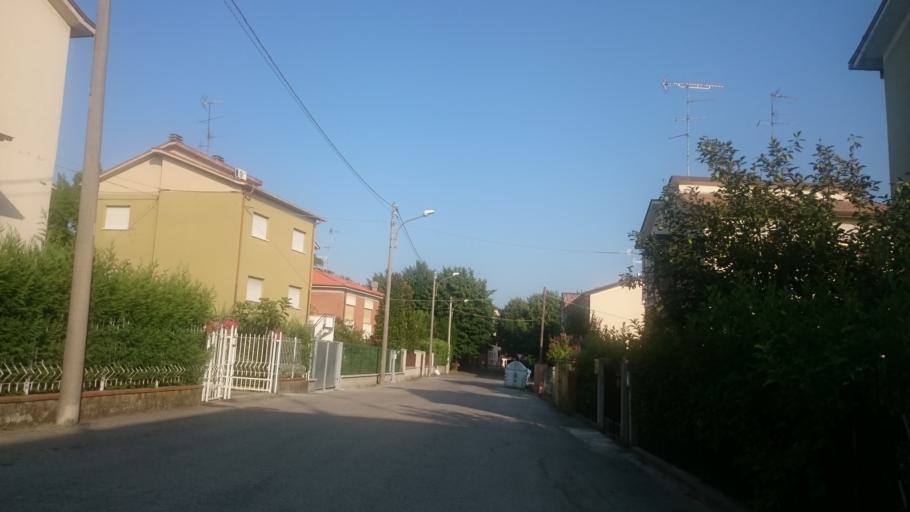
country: IT
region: Emilia-Romagna
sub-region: Provincia di Reggio Emilia
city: Scandiano
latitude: 44.5967
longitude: 10.6925
